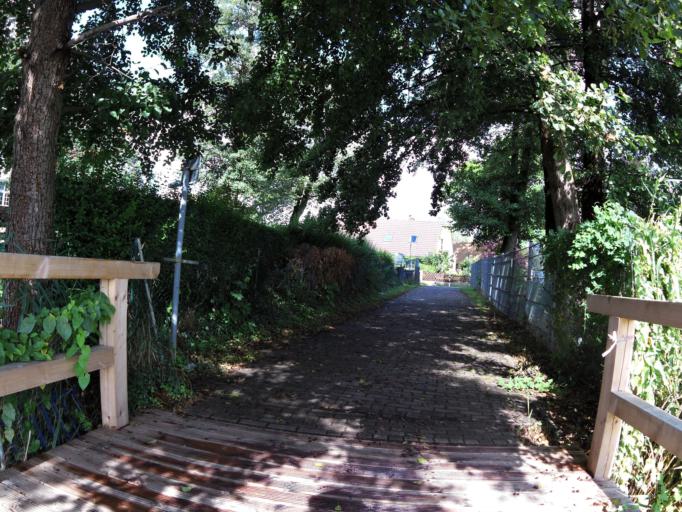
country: DE
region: Brandenburg
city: Storkow
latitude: 52.2590
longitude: 13.9416
